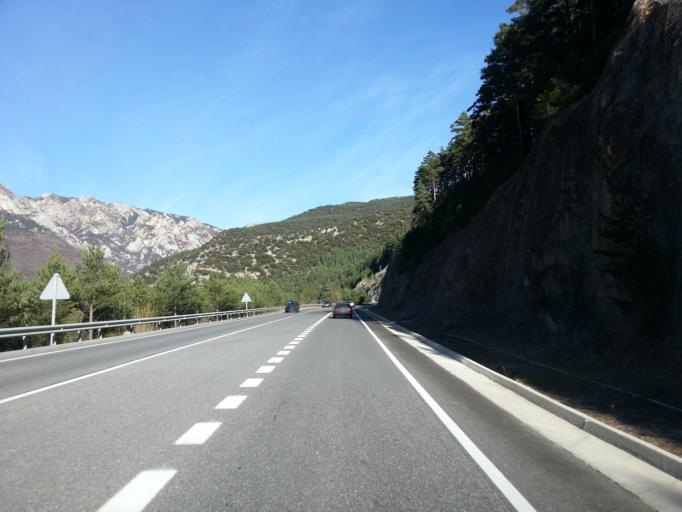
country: ES
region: Catalonia
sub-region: Provincia de Barcelona
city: Baga
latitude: 42.2667
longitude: 1.8523
